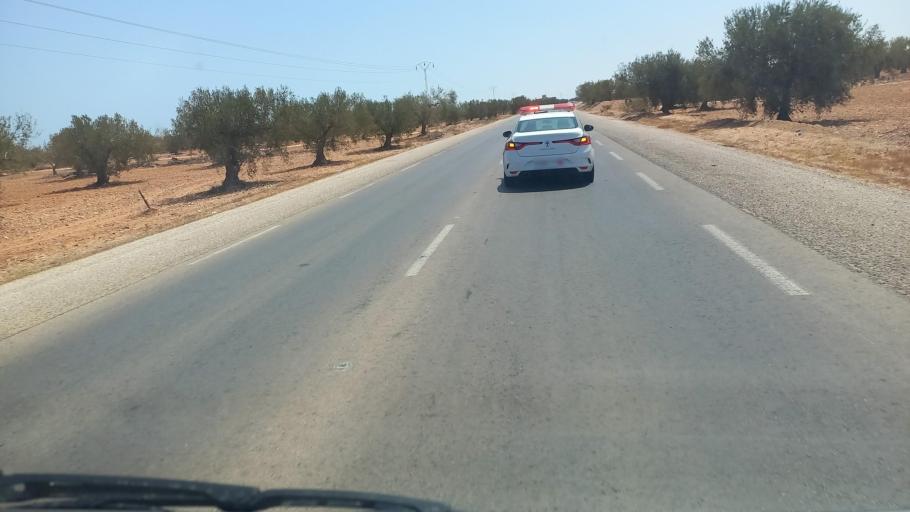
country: TN
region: Madanin
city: Zarzis
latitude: 33.5545
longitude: 11.0622
